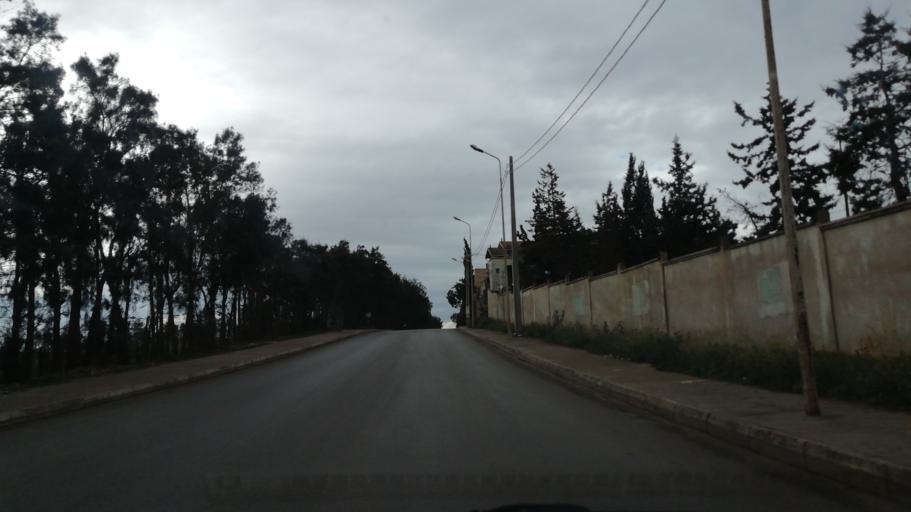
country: DZ
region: Oran
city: Oran
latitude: 35.6958
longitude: -0.5978
